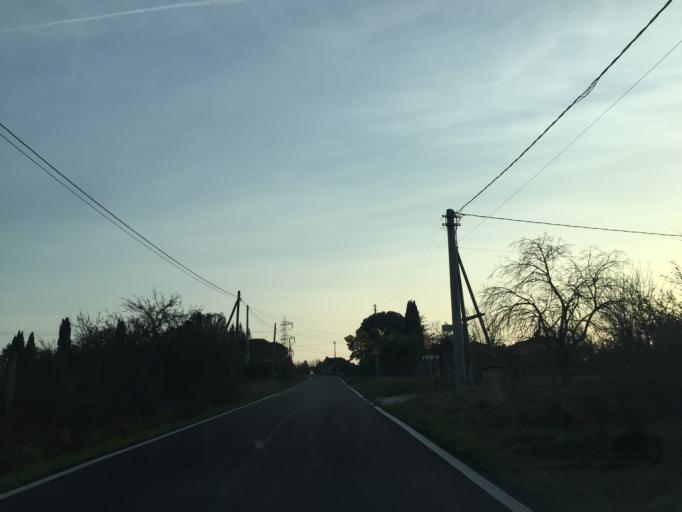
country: IT
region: Latium
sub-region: Citta metropolitana di Roma Capitale
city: Mazzano Romano
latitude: 42.1819
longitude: 12.3637
